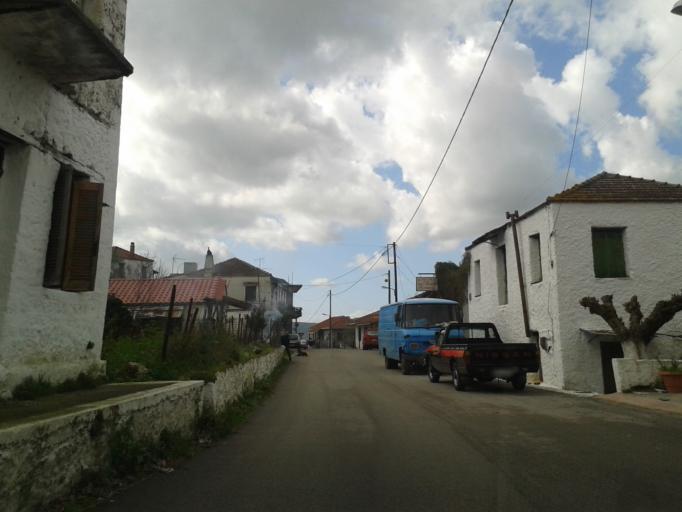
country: GR
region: West Greece
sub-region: Nomos Aitolias kai Akarnanias
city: Fitiai
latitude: 38.6433
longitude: 21.1819
